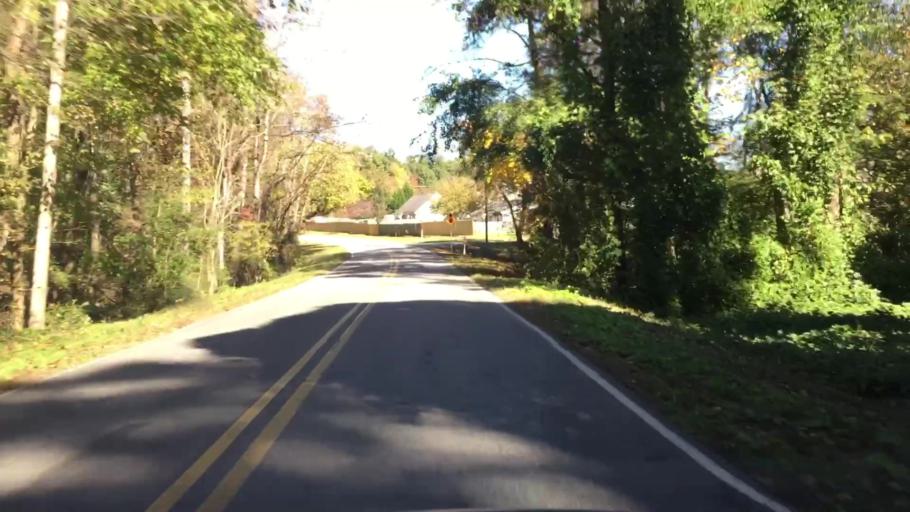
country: US
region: North Carolina
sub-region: Iredell County
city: Mooresville
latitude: 35.6059
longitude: -80.8020
